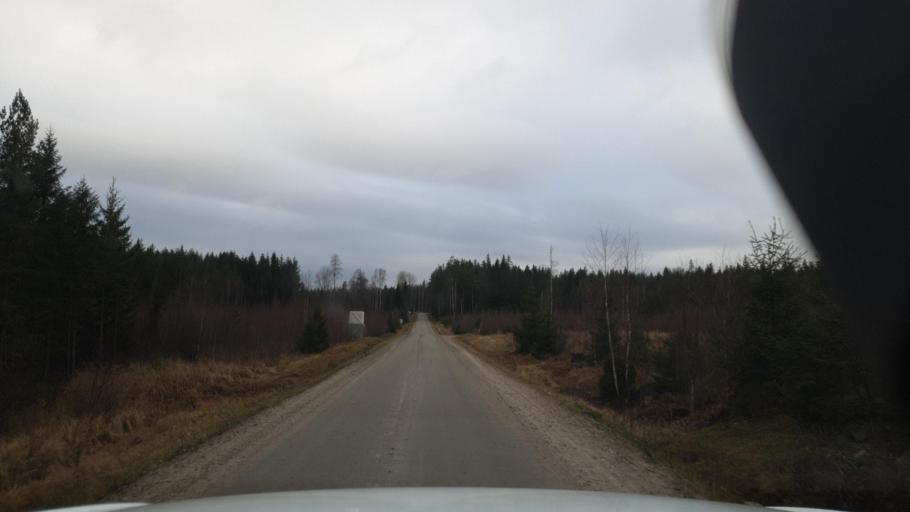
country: SE
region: Vaermland
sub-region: Karlstads Kommun
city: Edsvalla
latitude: 59.5205
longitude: 13.0059
